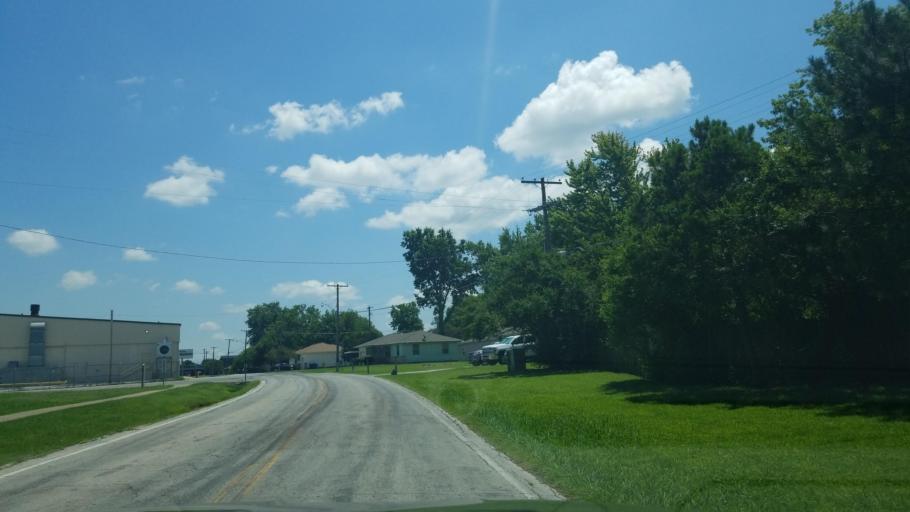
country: US
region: Oklahoma
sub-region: Tulsa County
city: Broken Arrow
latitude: 36.0503
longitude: -95.7835
